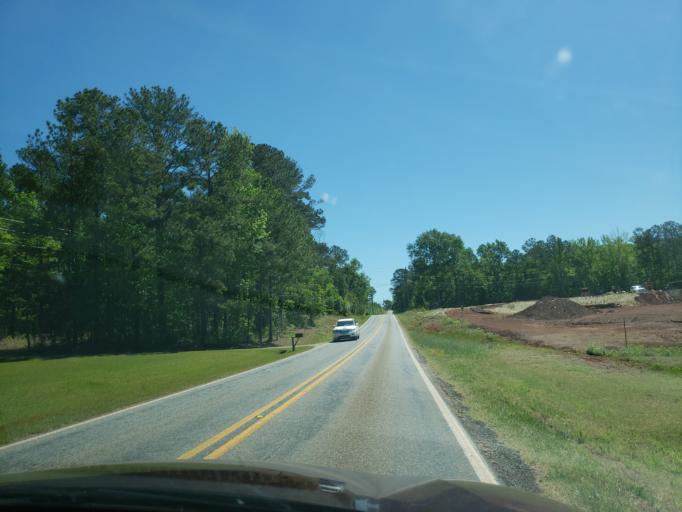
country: US
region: Alabama
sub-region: Tallapoosa County
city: Dadeville
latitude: 32.7080
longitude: -85.7990
